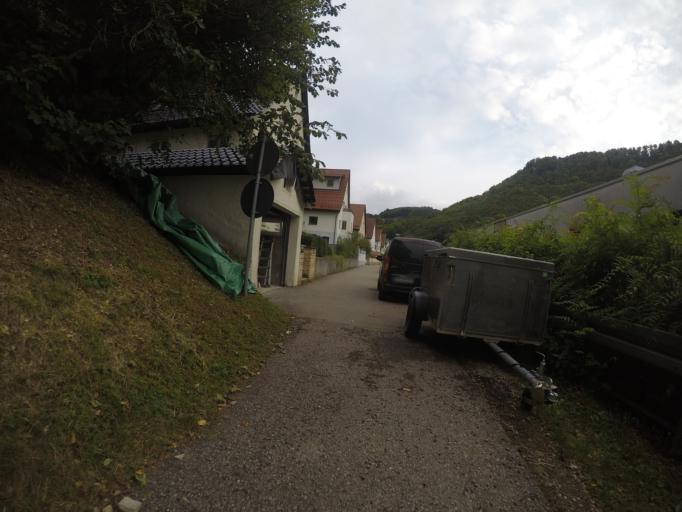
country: DE
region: Baden-Wuerttemberg
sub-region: Tuebingen Region
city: Pfullingen
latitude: 48.4110
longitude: 9.2642
